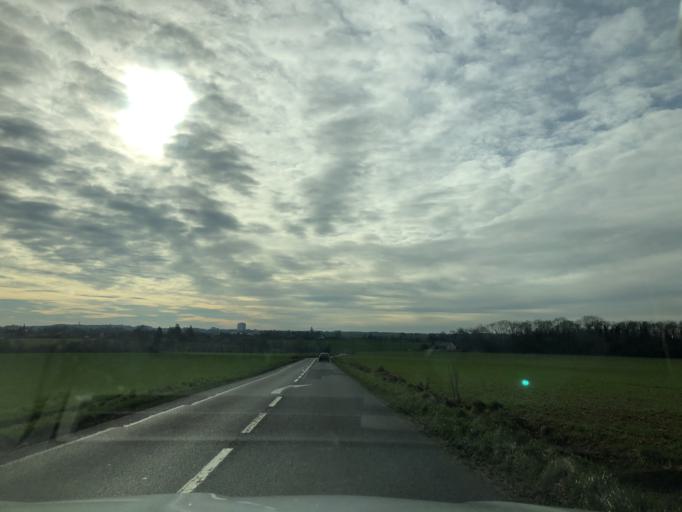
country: FR
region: Lower Normandy
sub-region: Departement du Calvados
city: Beuville
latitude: 49.2540
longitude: -0.3267
